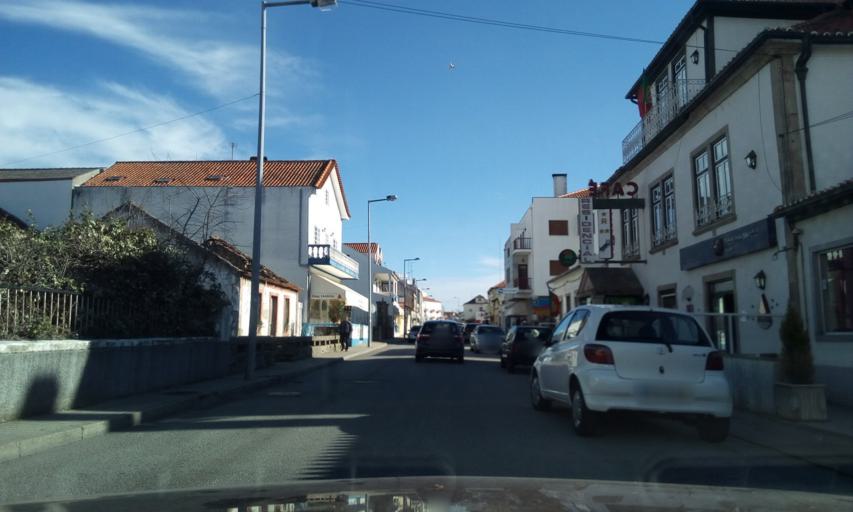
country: ES
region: Castille and Leon
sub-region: Provincia de Salamanca
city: Fuentes de Onoro
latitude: 40.6089
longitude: -6.8302
